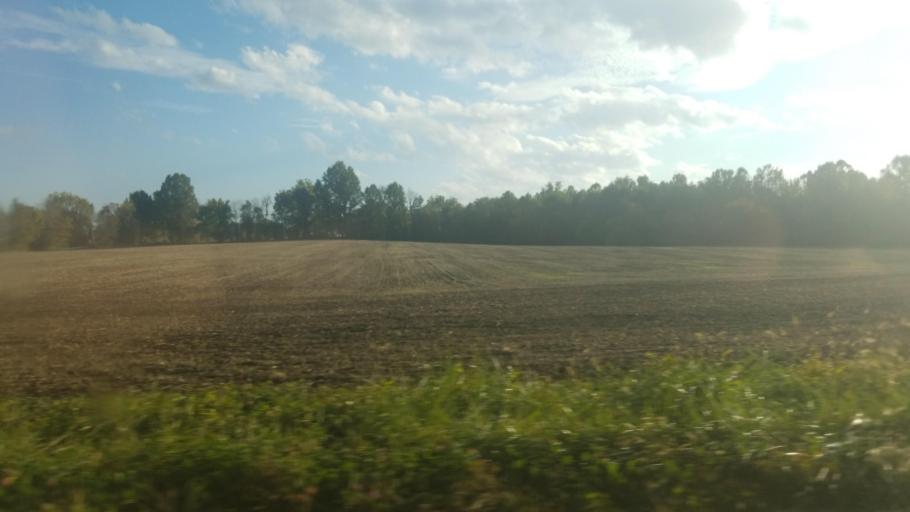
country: US
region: Illinois
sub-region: Saline County
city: Carrier Mills
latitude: 37.8051
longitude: -88.6850
